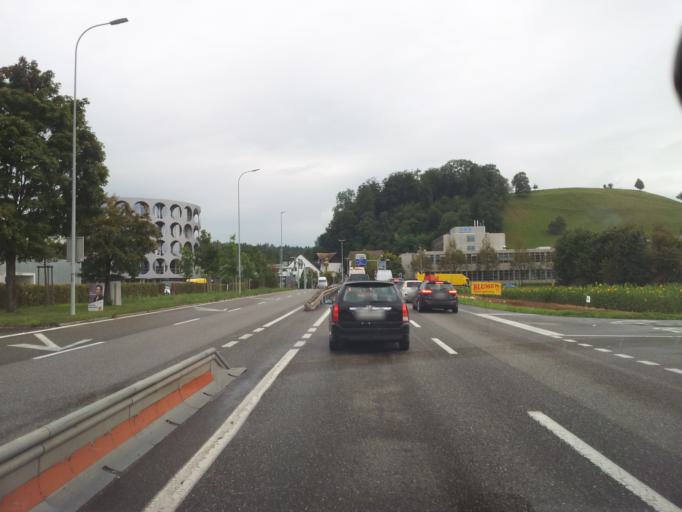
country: CH
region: Aargau
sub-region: Bezirk Lenzburg
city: Lenzburg
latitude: 47.3916
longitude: 8.1918
